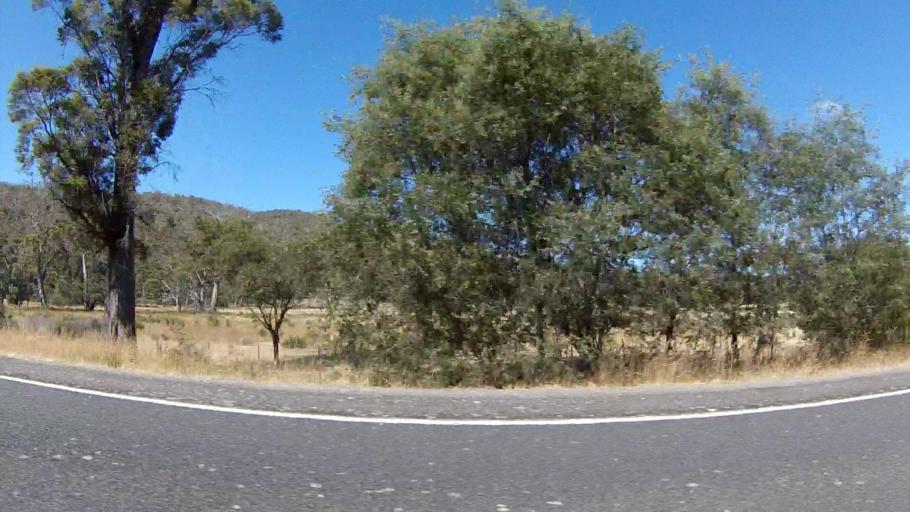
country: AU
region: Tasmania
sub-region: Sorell
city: Sorell
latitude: -42.5800
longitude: 147.8154
